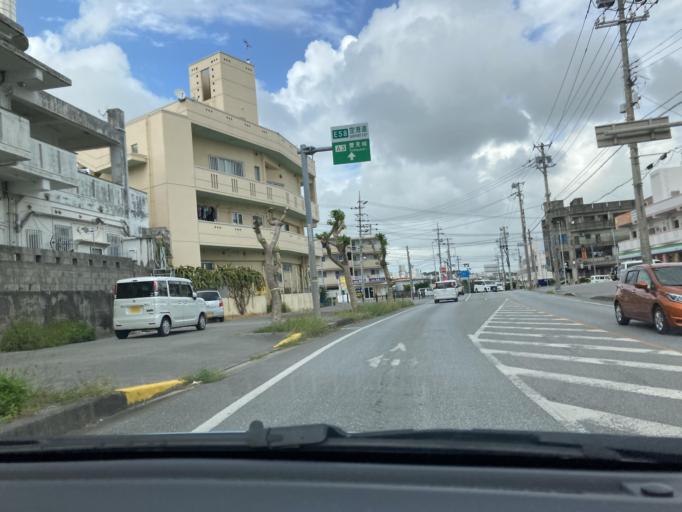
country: JP
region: Okinawa
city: Itoman
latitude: 26.1337
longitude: 127.6866
